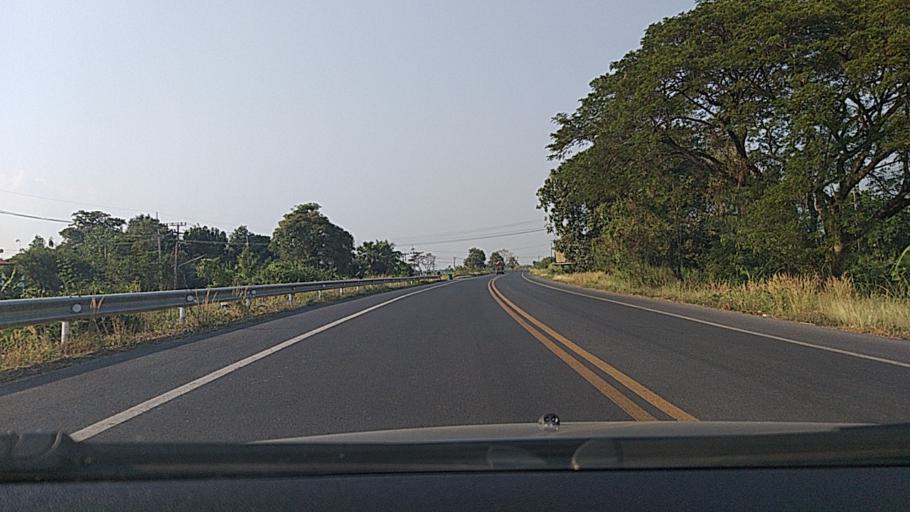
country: TH
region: Sing Buri
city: Phrom Buri
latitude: 14.8032
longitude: 100.4348
